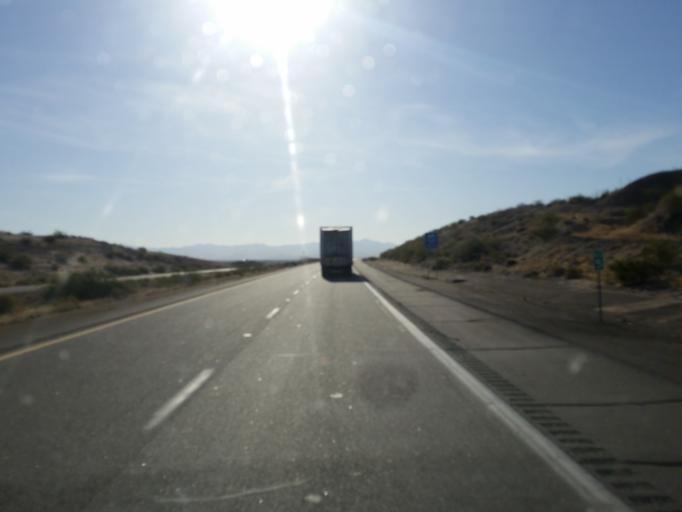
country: US
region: Arizona
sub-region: Mohave County
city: Desert Hills
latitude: 34.7261
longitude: -114.4009
